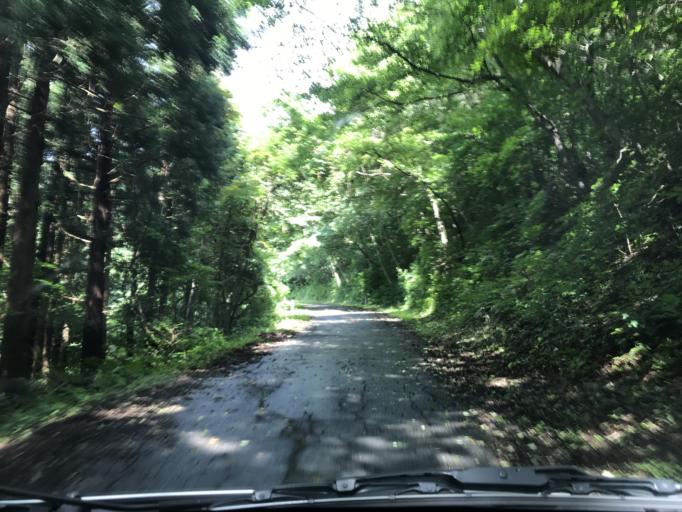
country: JP
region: Iwate
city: Ofunato
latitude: 38.9874
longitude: 141.4387
